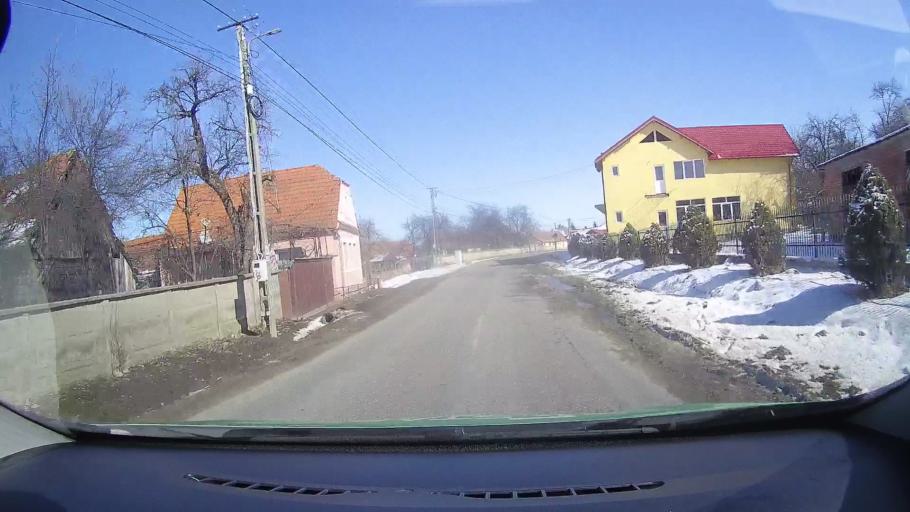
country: RO
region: Brasov
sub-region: Oras Victoria
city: Victoria
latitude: 45.7444
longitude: 24.7388
